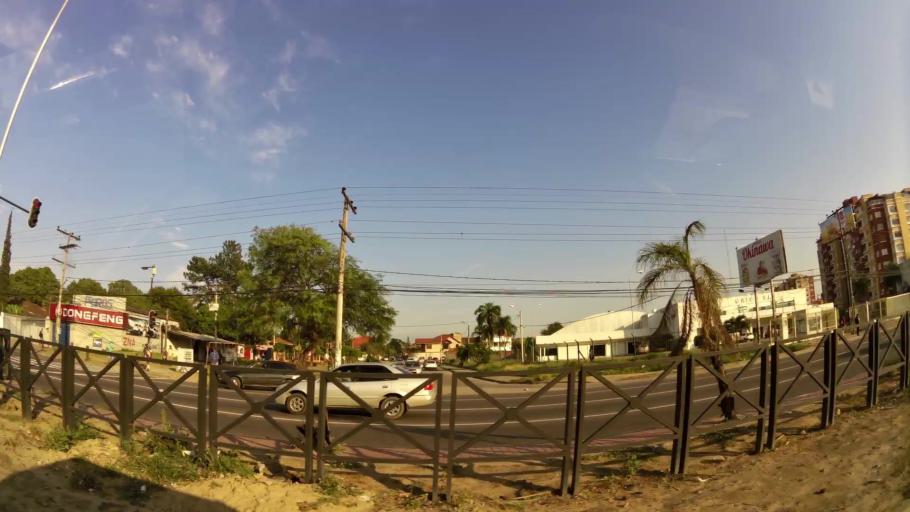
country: BO
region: Santa Cruz
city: Santa Cruz de la Sierra
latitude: -17.7444
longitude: -63.1731
